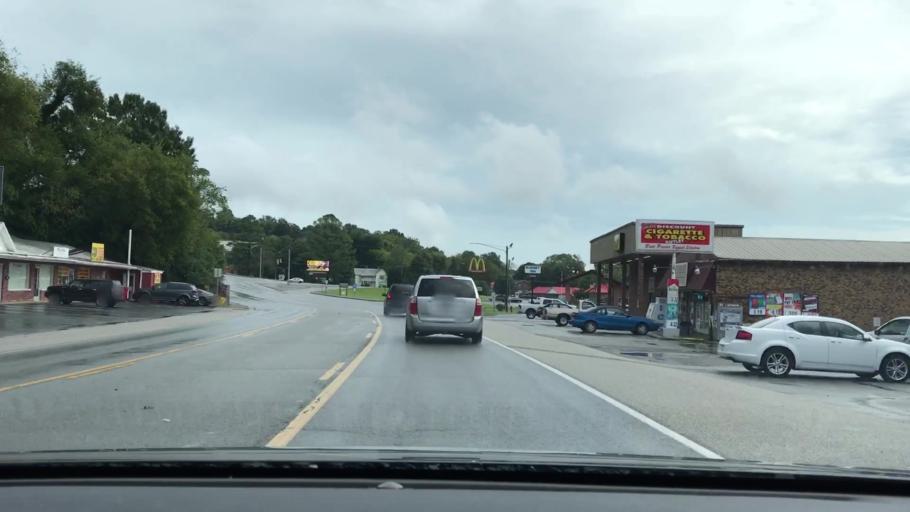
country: US
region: Tennessee
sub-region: Smith County
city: Carthage
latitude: 36.2622
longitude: -85.9537
